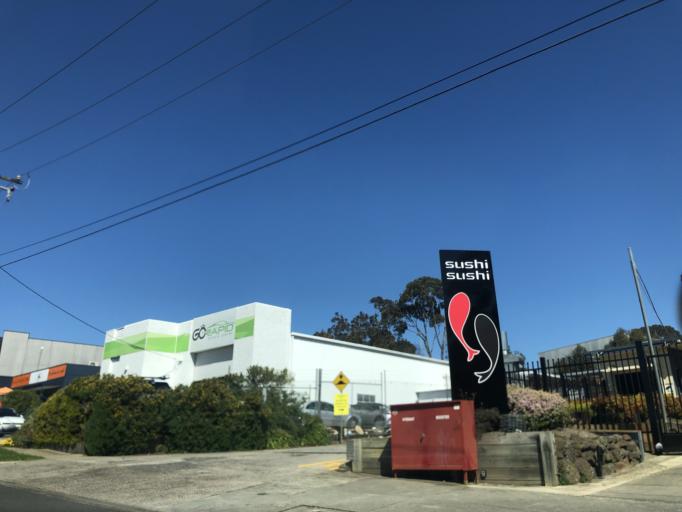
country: AU
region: Victoria
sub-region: Monash
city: Notting Hill
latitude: -37.8946
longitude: 145.1320
